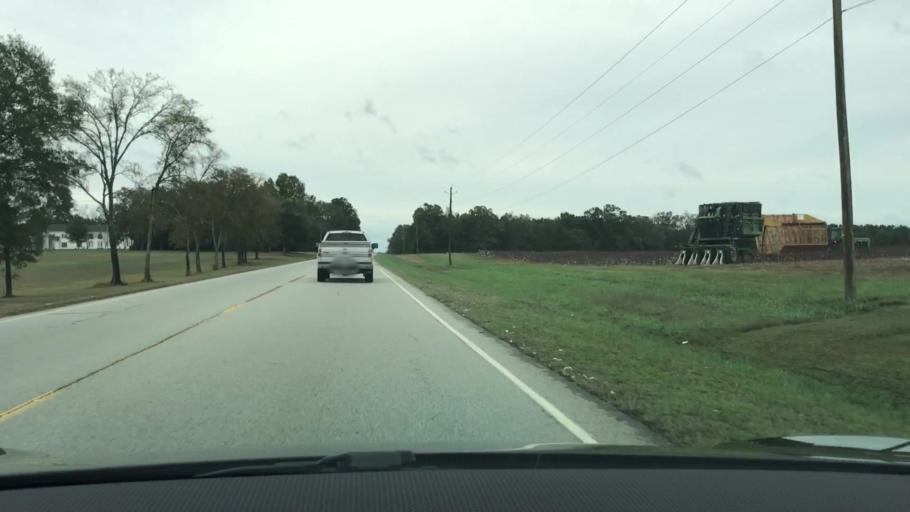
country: US
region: Georgia
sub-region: Warren County
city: Firing Range
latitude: 33.4267
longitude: -82.6834
